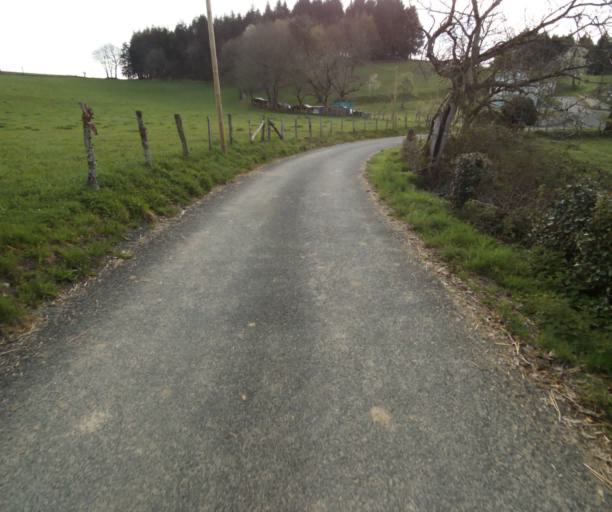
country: FR
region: Limousin
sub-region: Departement de la Correze
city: Correze
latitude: 45.3558
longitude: 1.8450
